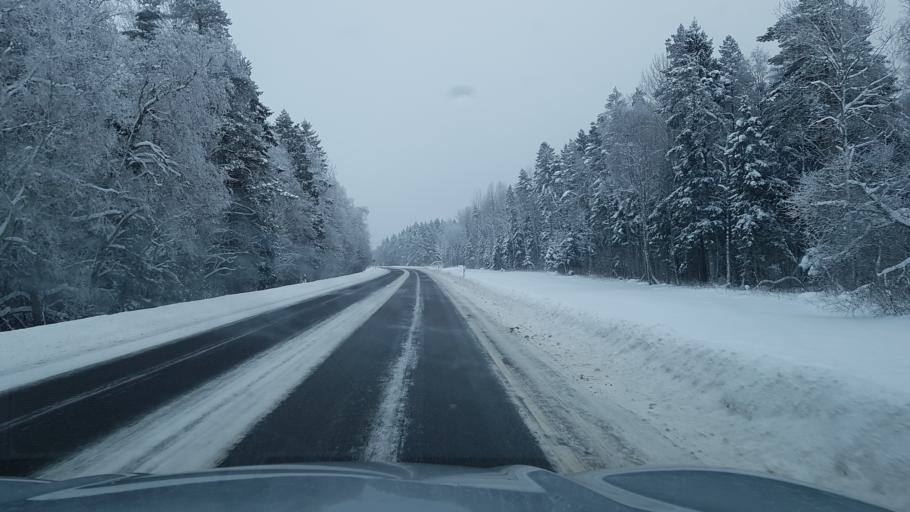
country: EE
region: Ida-Virumaa
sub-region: Johvi vald
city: Johvi
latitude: 59.3077
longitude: 27.3930
